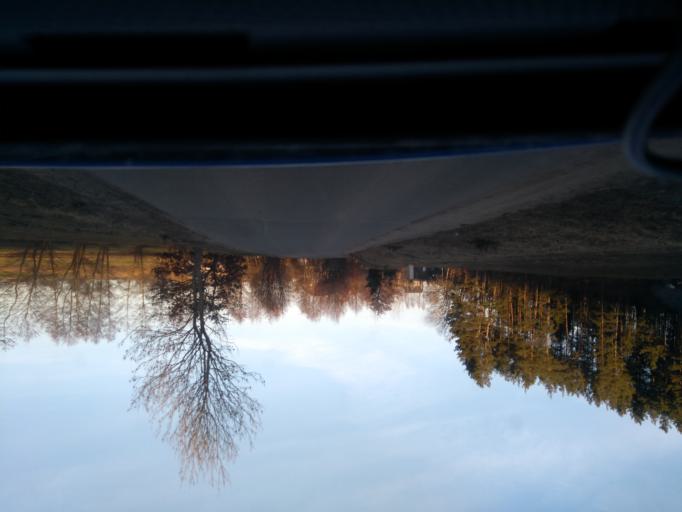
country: PL
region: Pomeranian Voivodeship
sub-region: Powiat kartuski
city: Przodkowo
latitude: 54.3820
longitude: 18.2674
